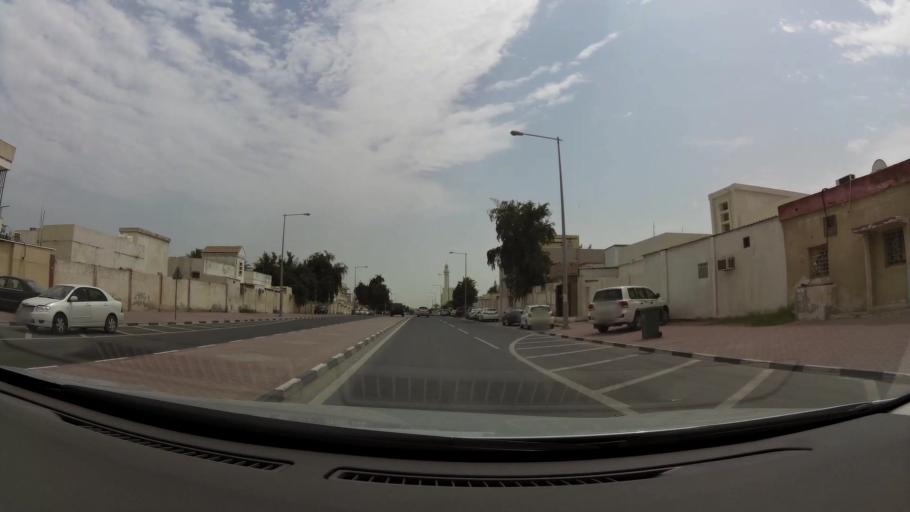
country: QA
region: Baladiyat ar Rayyan
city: Ar Rayyan
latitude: 25.3312
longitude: 51.4704
